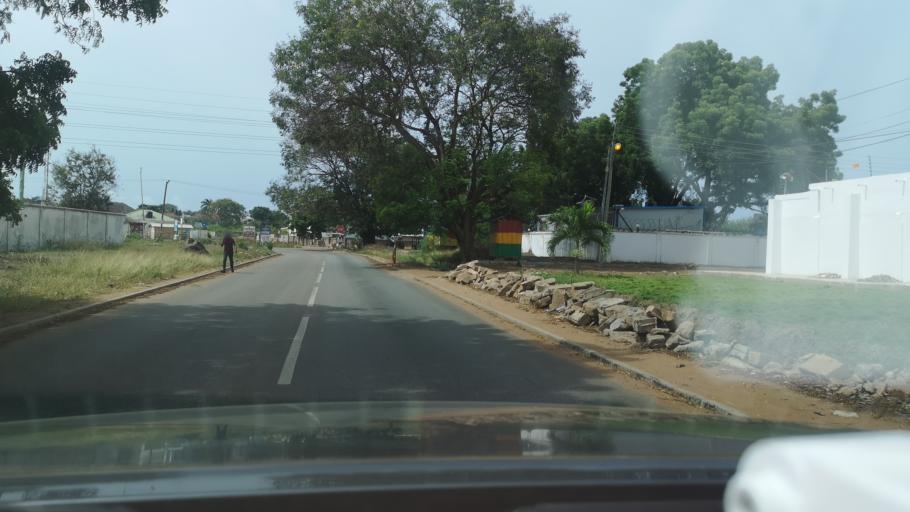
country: GH
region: Greater Accra
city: Tema
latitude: 5.6552
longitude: -0.0222
